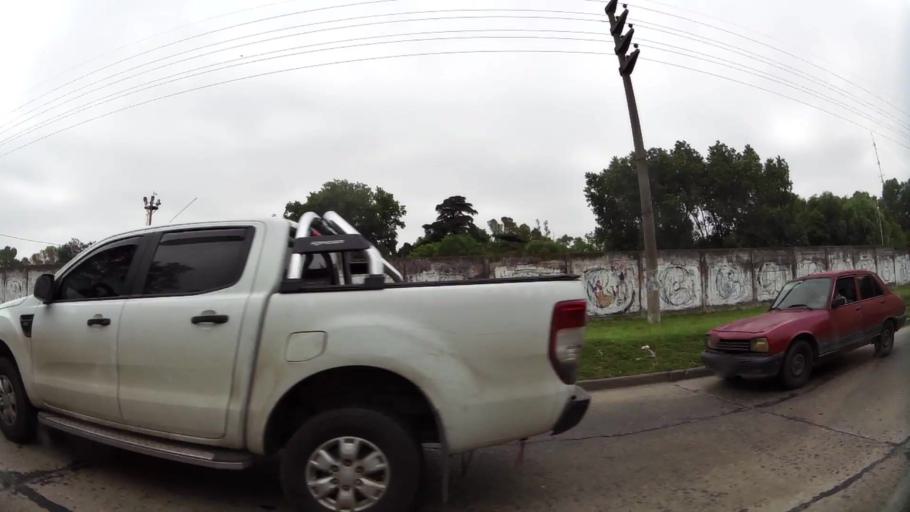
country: AR
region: Buenos Aires
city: San Justo
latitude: -34.7022
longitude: -58.5440
